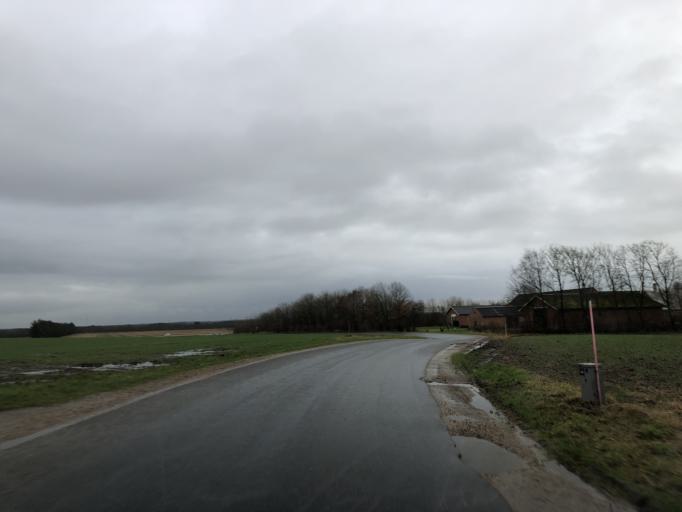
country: DK
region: Central Jutland
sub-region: Holstebro Kommune
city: Holstebro
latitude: 56.3742
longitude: 8.7288
